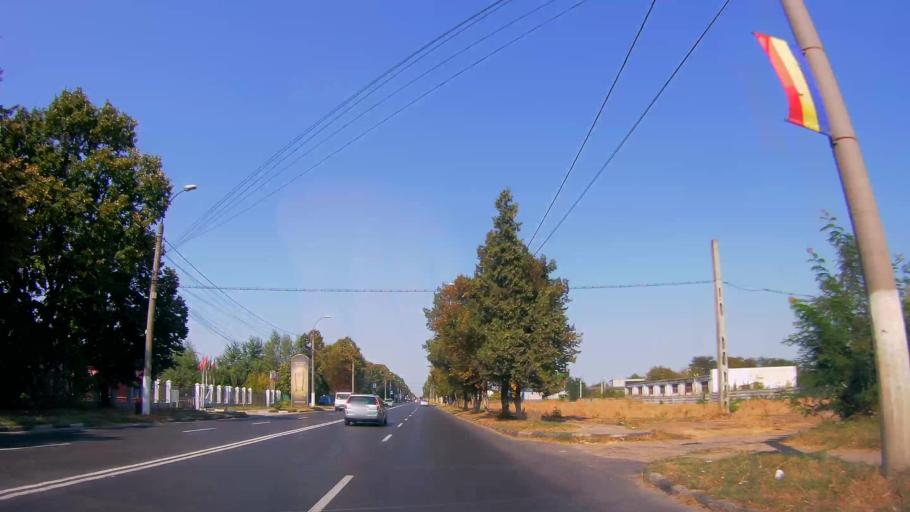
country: RO
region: Giurgiu
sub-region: Comuna Fratesti
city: Remus
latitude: 43.9204
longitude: 25.9732
